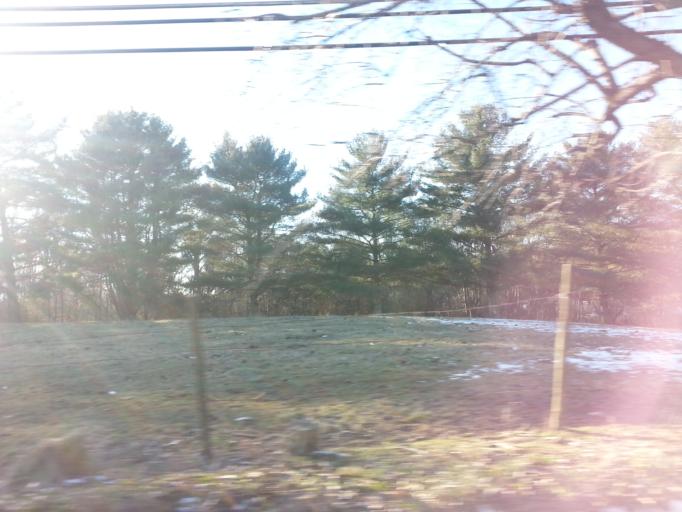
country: US
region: Tennessee
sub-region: Knox County
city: Farragut
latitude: 35.9606
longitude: -84.0593
